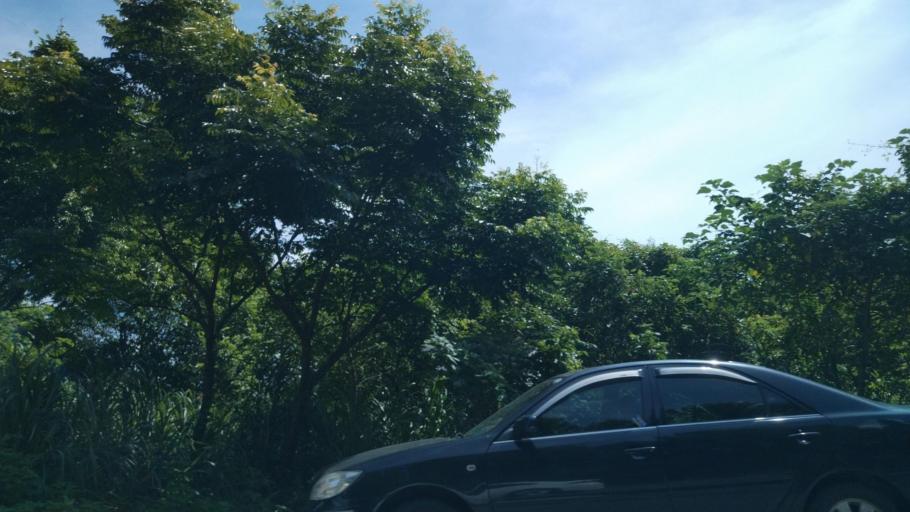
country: TW
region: Taipei
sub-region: Taipei
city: Banqiao
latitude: 24.9409
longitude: 121.5053
